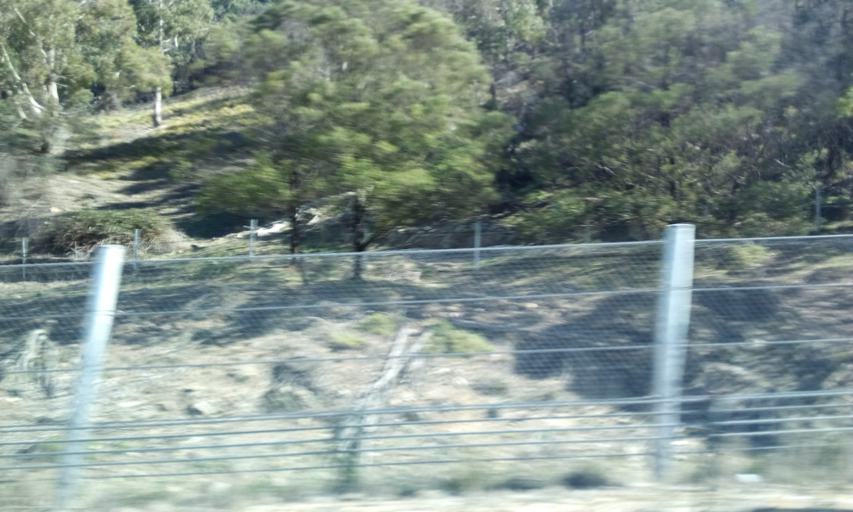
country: AU
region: New South Wales
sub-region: Yass Valley
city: Gundaroo
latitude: -35.0531
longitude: 149.3753
